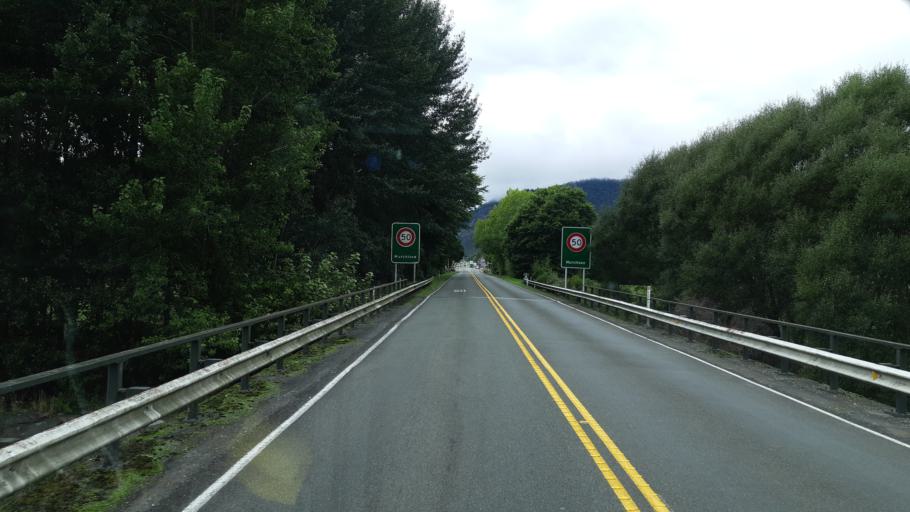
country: NZ
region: West Coast
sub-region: Buller District
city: Westport
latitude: -41.8001
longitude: 172.3196
